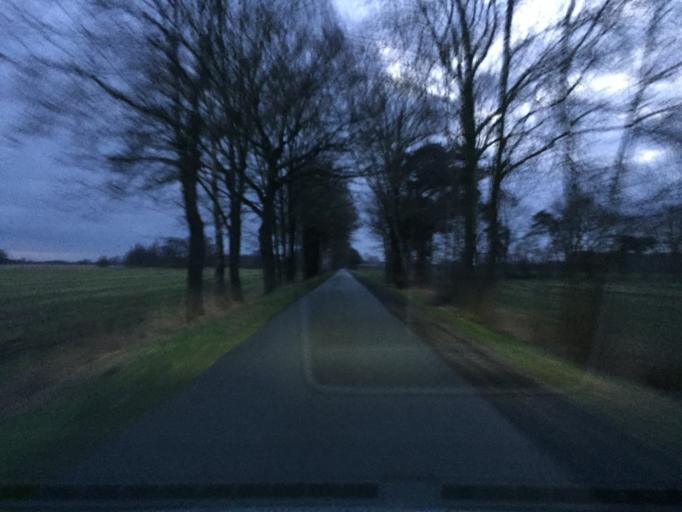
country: DE
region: Lower Saxony
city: Kirchdorf
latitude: 52.6329
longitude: 8.8565
